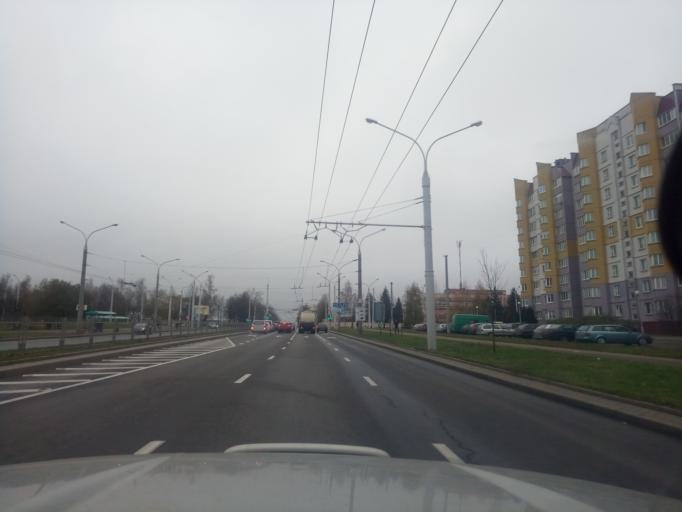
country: BY
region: Minsk
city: Novoye Medvezhino
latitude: 53.8800
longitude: 27.4842
